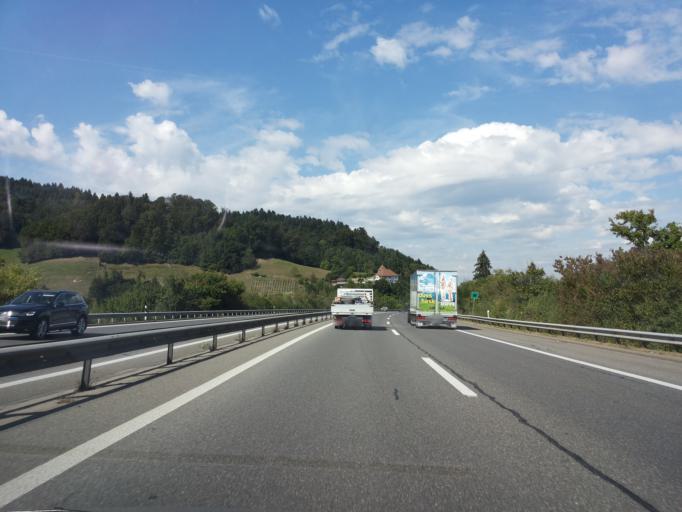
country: CH
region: Lucerne
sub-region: Willisau District
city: Dagmersellen
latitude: 47.2133
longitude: 7.9763
